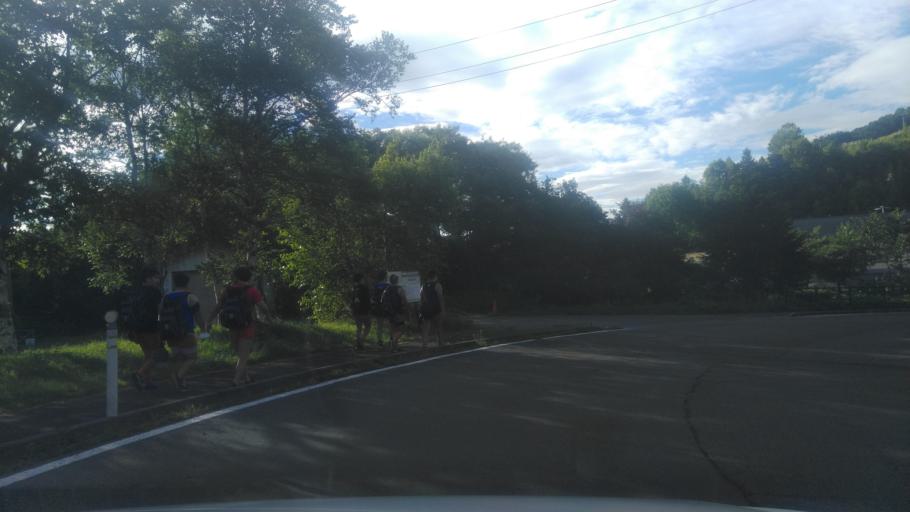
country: JP
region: Nagano
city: Suzaka
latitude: 36.5305
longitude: 138.3454
